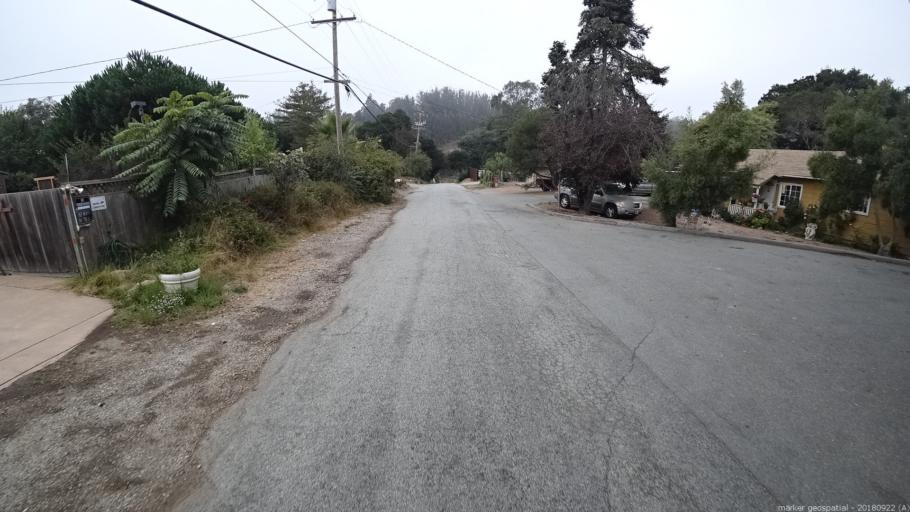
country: US
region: California
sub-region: Monterey County
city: Prunedale
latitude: 36.7878
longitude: -121.6687
